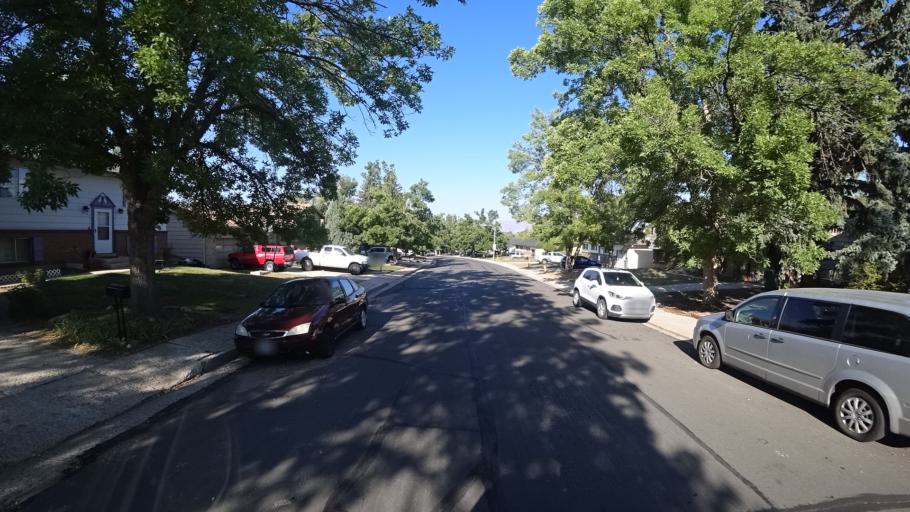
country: US
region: Colorado
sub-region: El Paso County
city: Cimarron Hills
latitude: 38.8813
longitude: -104.7330
